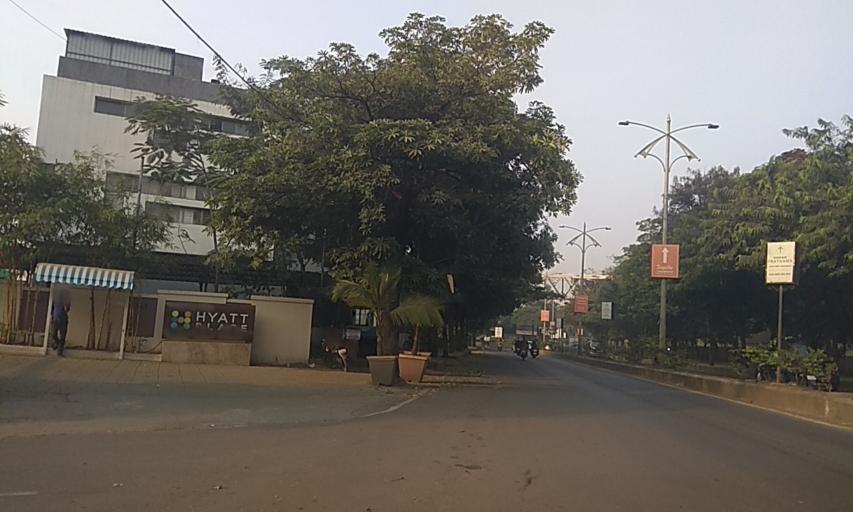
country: IN
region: Maharashtra
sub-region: Pune Division
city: Pimpri
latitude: 18.5864
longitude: 73.7361
